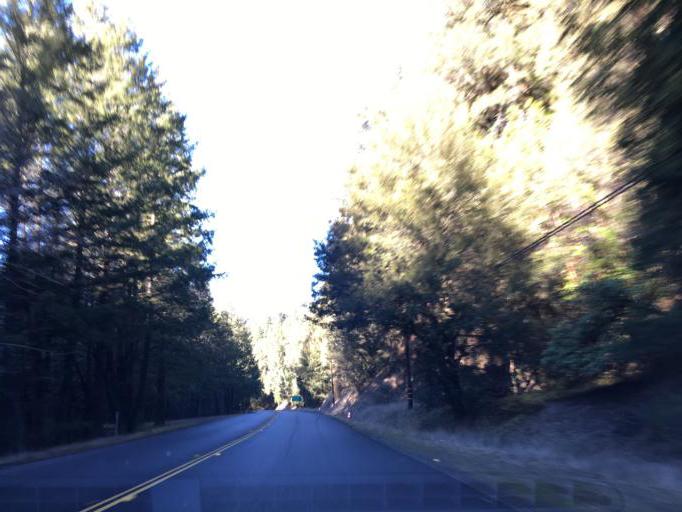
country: US
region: California
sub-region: Mendocino County
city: Laytonville
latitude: 39.8006
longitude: -123.5431
